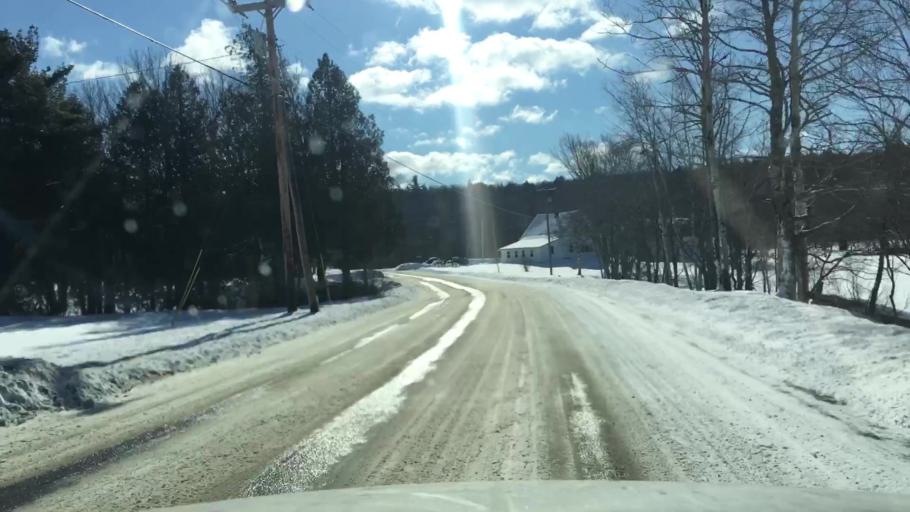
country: US
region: Maine
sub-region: Washington County
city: Calais
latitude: 45.0638
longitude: -67.4713
